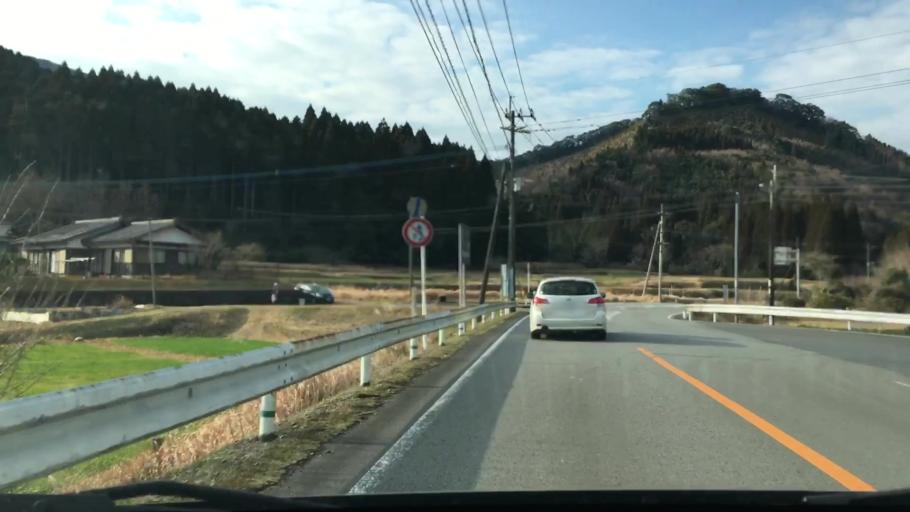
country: JP
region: Miyazaki
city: Nichinan
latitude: 31.7449
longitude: 131.3366
